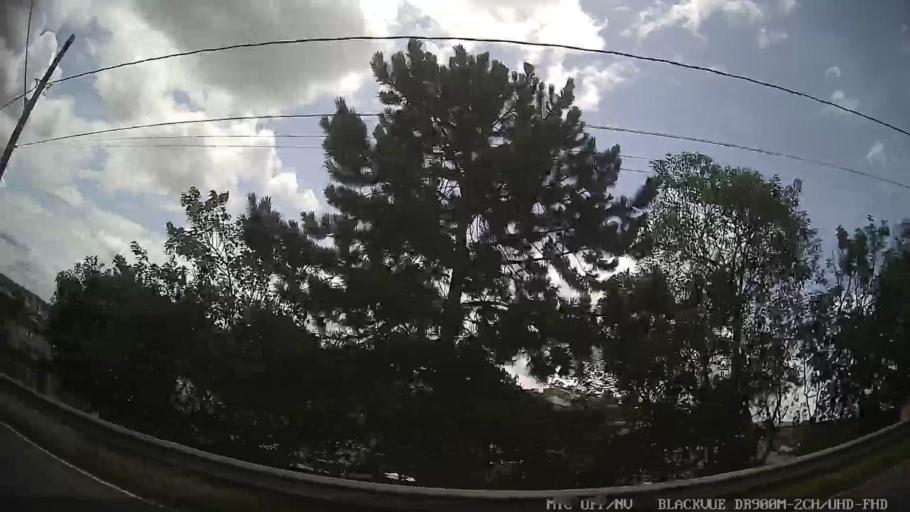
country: BR
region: Sao Paulo
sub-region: Mogi das Cruzes
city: Mogi das Cruzes
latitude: -23.5681
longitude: -46.2154
